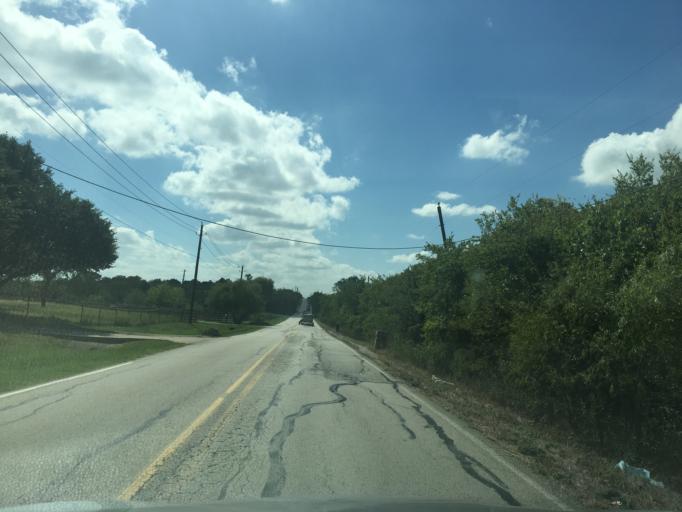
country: US
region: Texas
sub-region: Dallas County
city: Sachse
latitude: 32.9651
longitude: -96.5705
